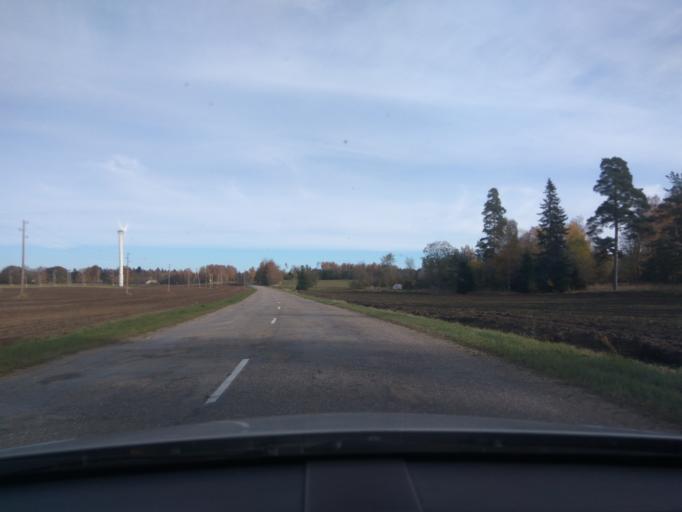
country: LV
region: Alsunga
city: Alsunga
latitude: 56.9900
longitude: 21.6134
